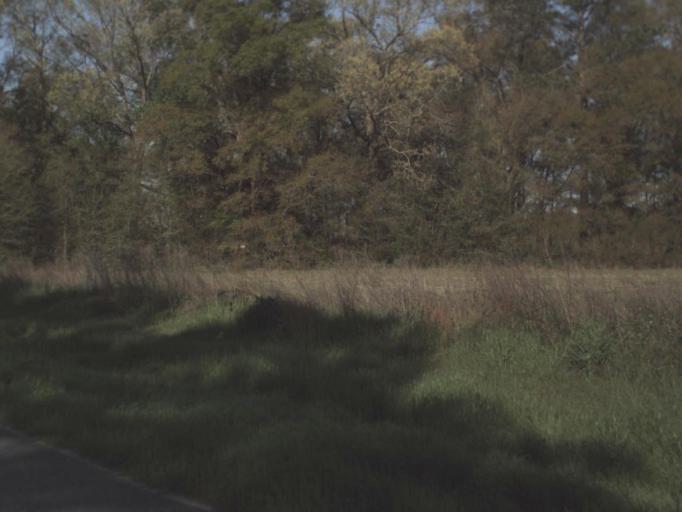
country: US
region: Florida
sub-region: Jackson County
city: Malone
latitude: 30.9726
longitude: -85.0959
